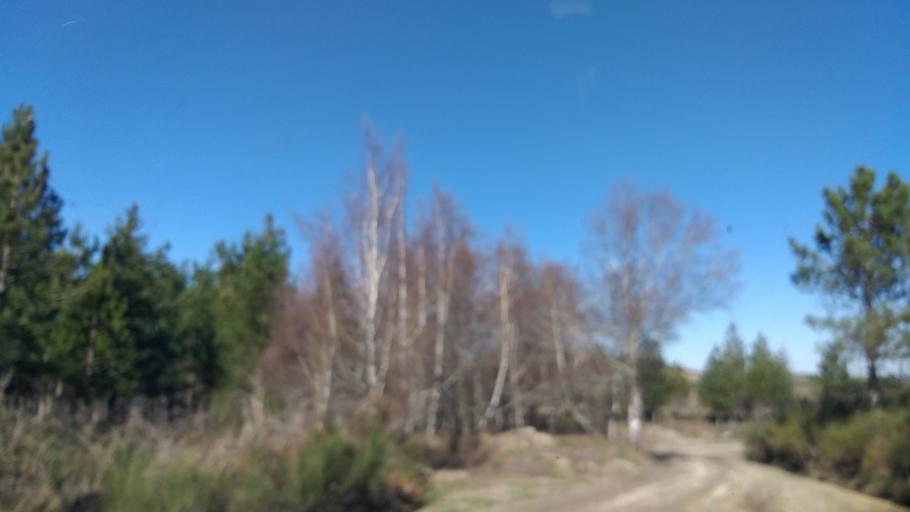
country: PT
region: Guarda
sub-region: Manteigas
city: Manteigas
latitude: 40.4958
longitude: -7.4925
